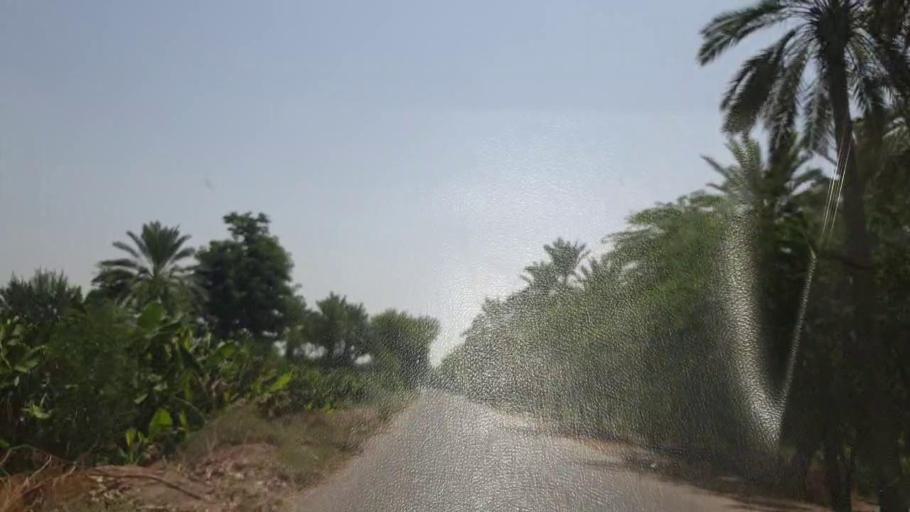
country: PK
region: Sindh
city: Kot Diji
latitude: 27.2830
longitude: 68.6322
